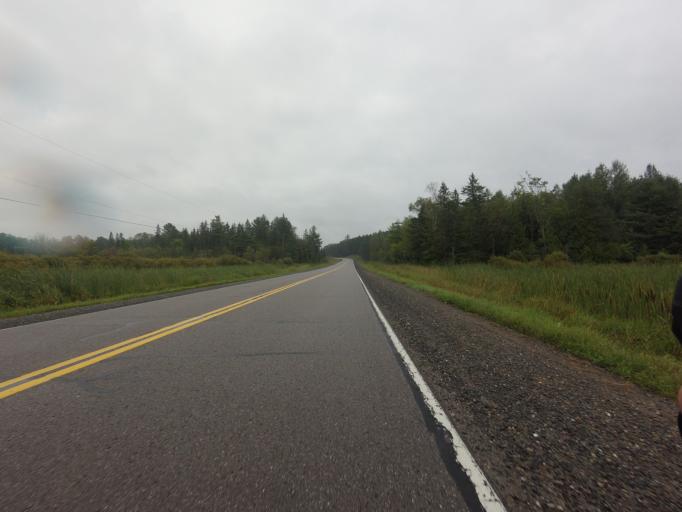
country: CA
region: Ontario
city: Perth
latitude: 45.0875
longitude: -76.4189
